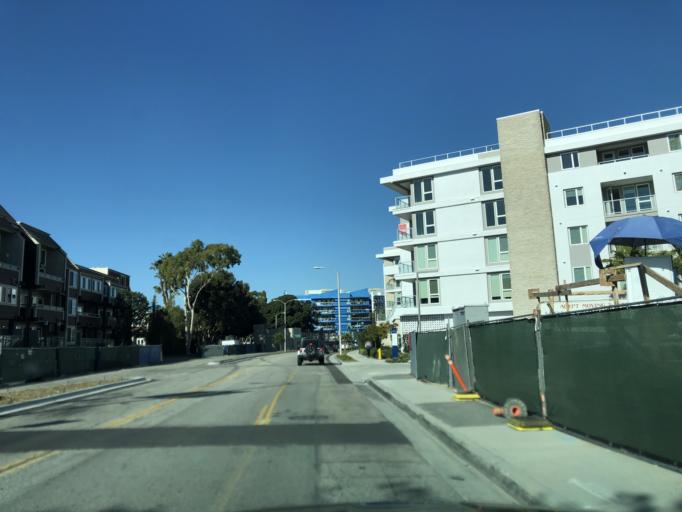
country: US
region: California
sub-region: Los Angeles County
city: Marina del Rey
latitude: 33.9748
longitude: -118.4581
